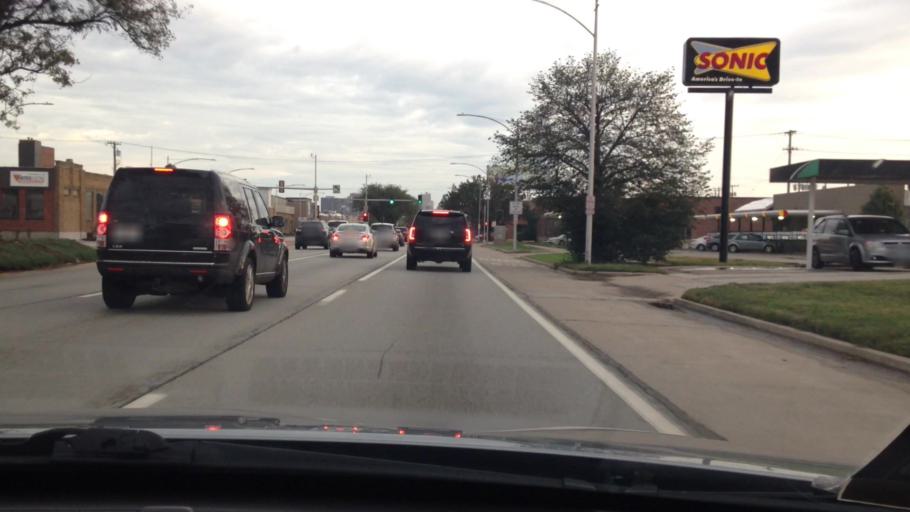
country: US
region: Missouri
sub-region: Clay County
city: North Kansas City
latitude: 39.1353
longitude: -94.5807
